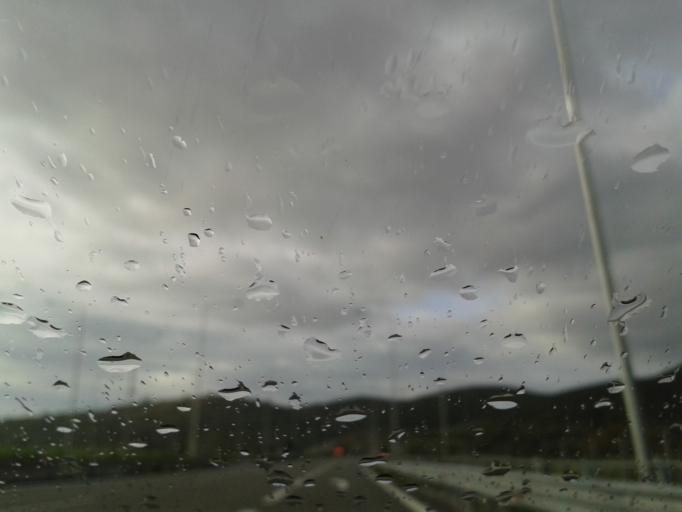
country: GR
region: West Greece
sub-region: Nomos Aitolias kai Akarnanias
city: Galatas
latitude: 38.3854
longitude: 21.5420
